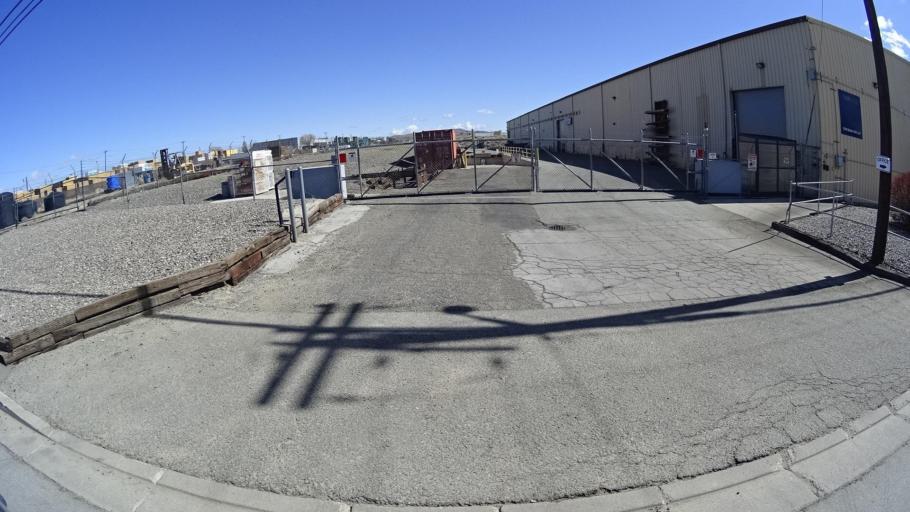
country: US
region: Nevada
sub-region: Washoe County
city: Lemmon Valley
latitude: 39.6576
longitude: -119.8830
